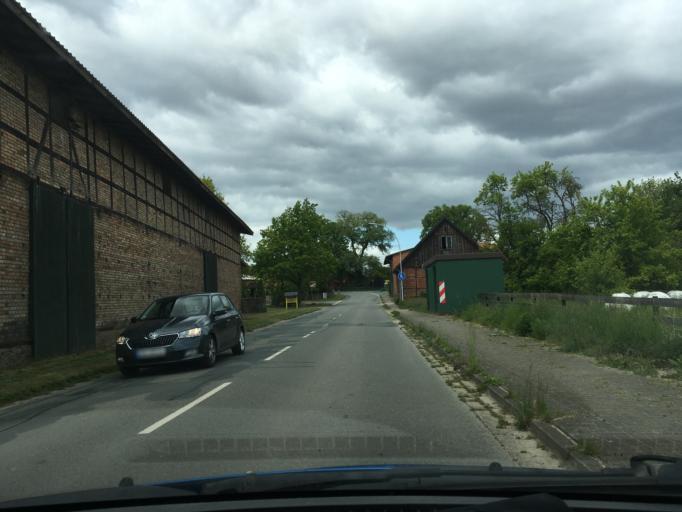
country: DE
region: Lower Saxony
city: Gerdau
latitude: 52.9208
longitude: 10.4149
